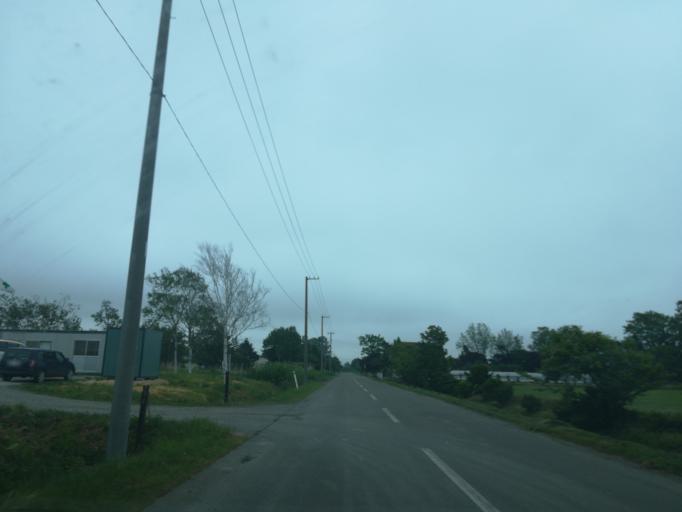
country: JP
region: Hokkaido
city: Ebetsu
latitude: 43.0697
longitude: 141.6413
